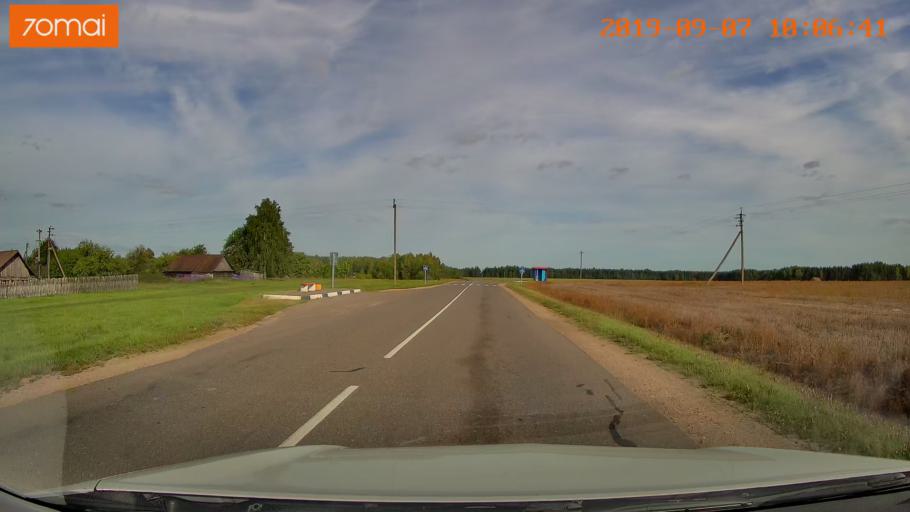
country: BY
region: Grodnenskaya
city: Voranava
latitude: 54.0653
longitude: 25.4023
